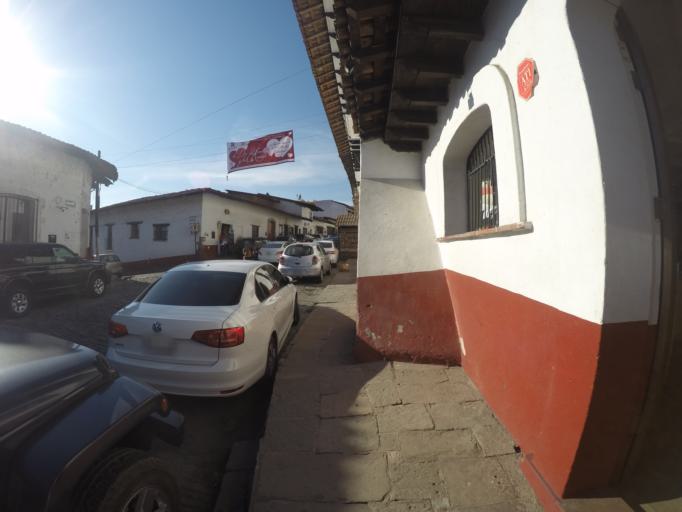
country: MX
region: Mexico
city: Valle de Bravo
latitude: 19.1900
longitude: -100.1290
